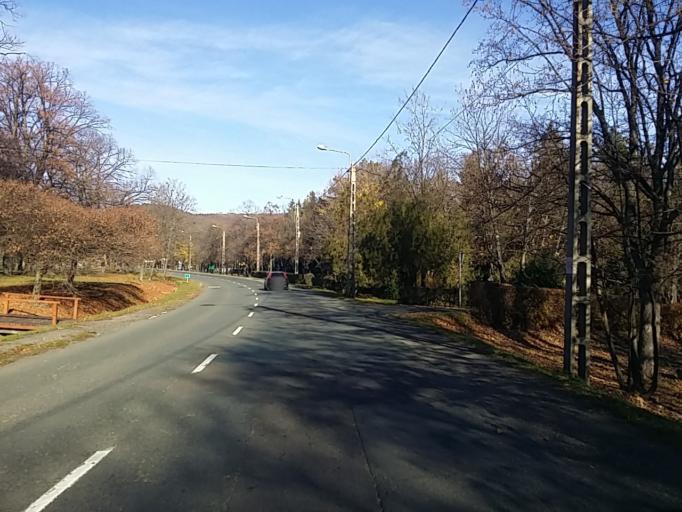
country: HU
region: Heves
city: Gyongyossolymos
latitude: 47.8286
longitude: 19.9713
